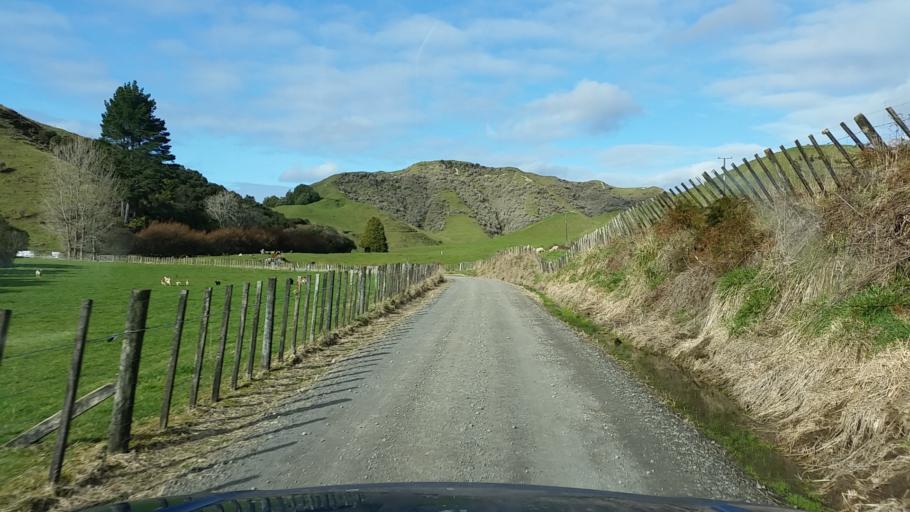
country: NZ
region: Taranaki
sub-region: South Taranaki District
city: Eltham
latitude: -39.2605
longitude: 174.5780
